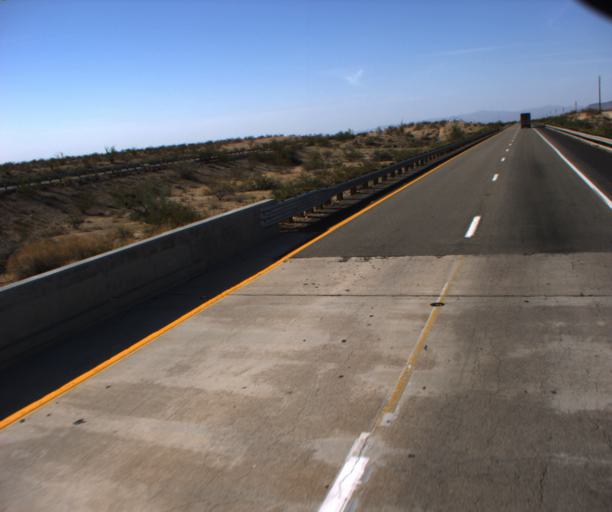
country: US
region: Arizona
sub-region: Mohave County
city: Kingman
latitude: 34.9636
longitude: -114.1439
